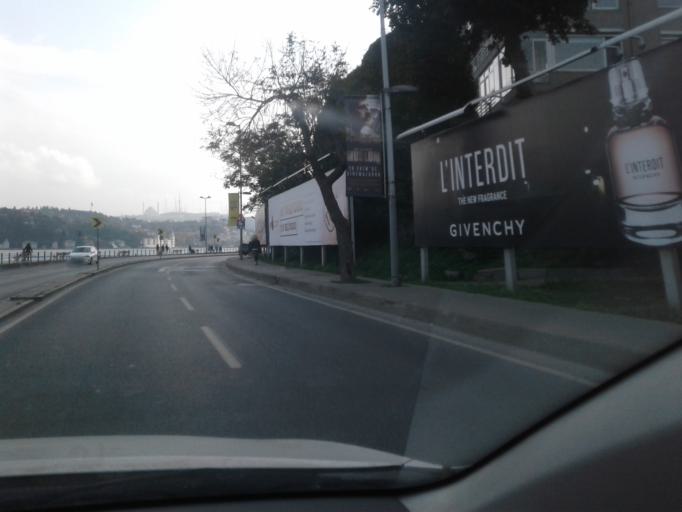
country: TR
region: Istanbul
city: UEskuedar
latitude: 41.0698
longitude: 29.0459
